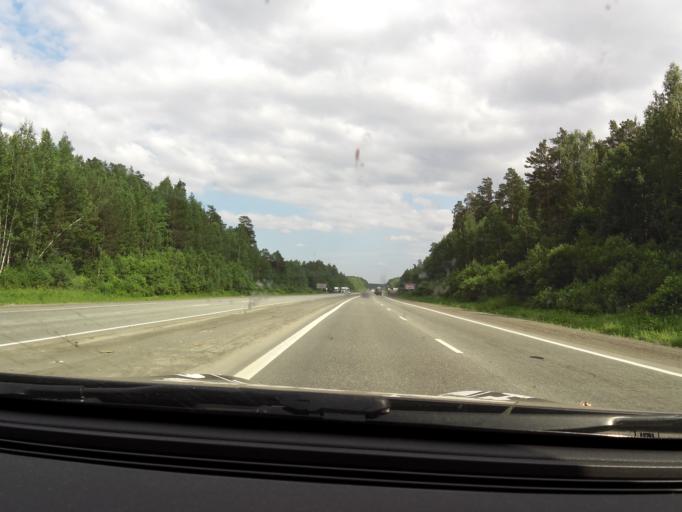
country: RU
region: Sverdlovsk
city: Talitsa
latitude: 56.8466
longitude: 60.0811
